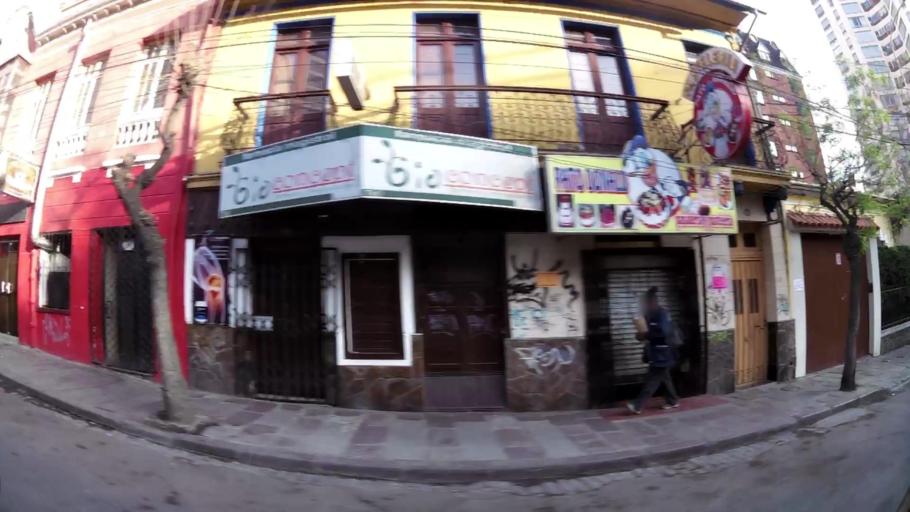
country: BO
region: La Paz
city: La Paz
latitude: -16.5077
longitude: -68.1300
